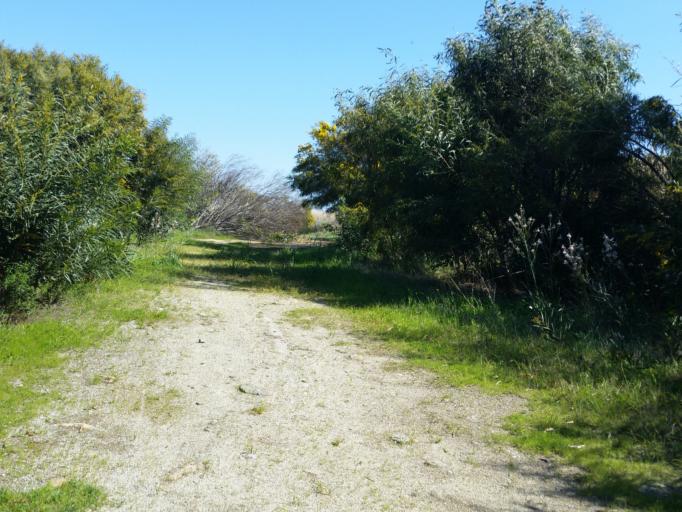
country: IT
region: Sardinia
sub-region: Provincia di Olbia-Tempio
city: Budoni
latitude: 40.7185
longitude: 9.7114
